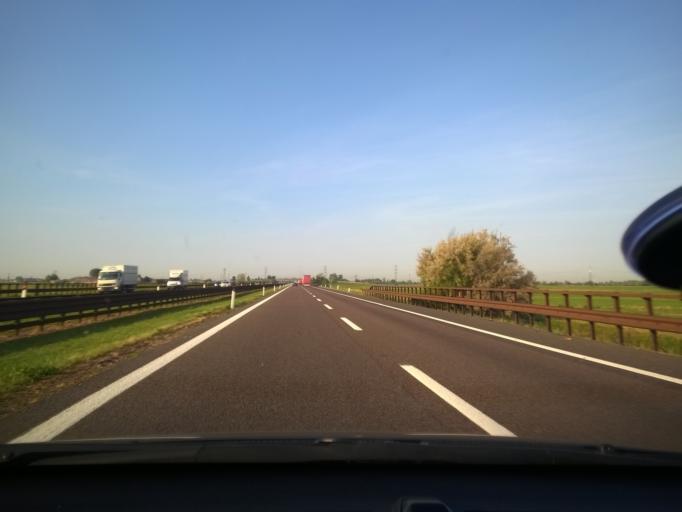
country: IT
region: Lombardy
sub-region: Provincia di Mantova
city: Castelbelforte
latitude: 45.2189
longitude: 10.8539
